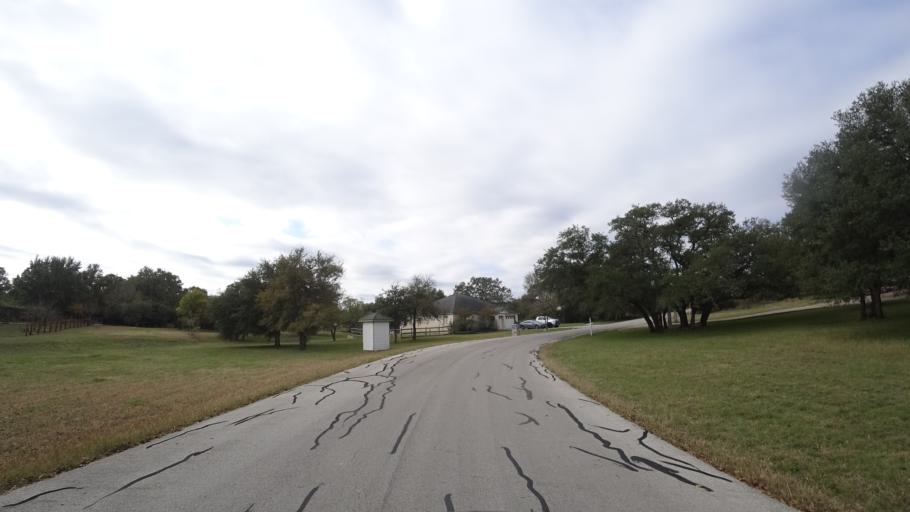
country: US
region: Texas
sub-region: Travis County
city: Shady Hollow
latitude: 30.1363
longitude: -97.8955
